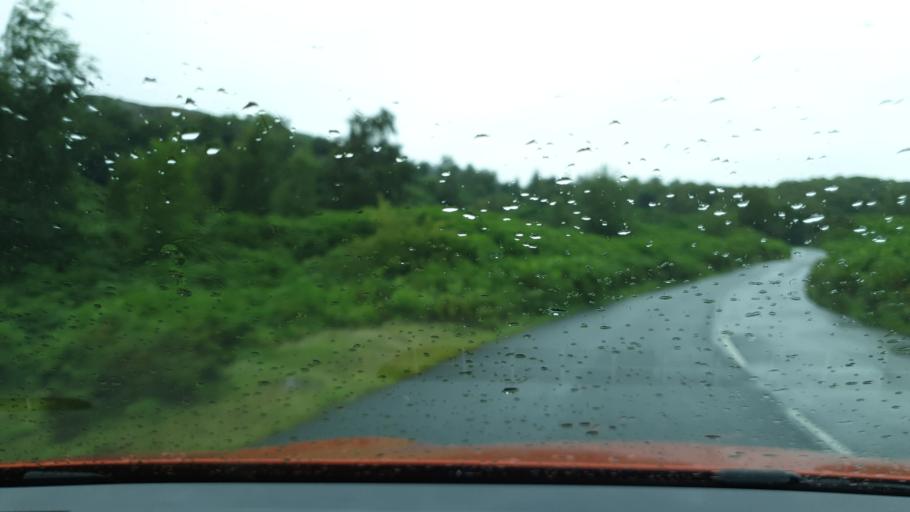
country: GB
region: England
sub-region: Cumbria
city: Ulverston
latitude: 54.3018
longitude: -3.0982
